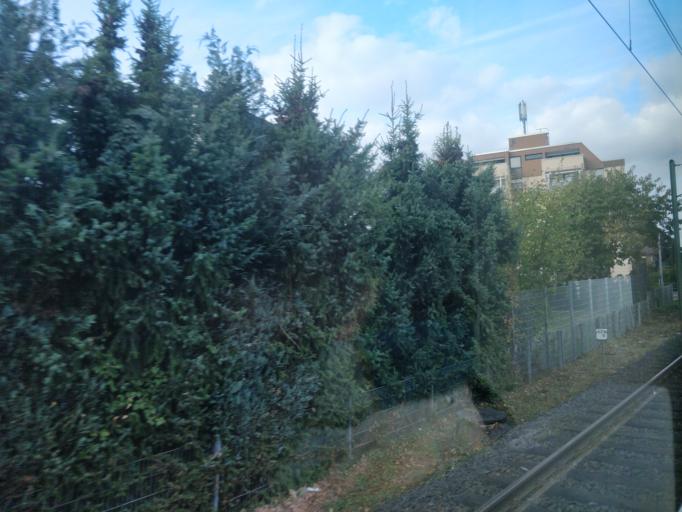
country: DE
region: North Rhine-Westphalia
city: Sankt Augustin
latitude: 50.7796
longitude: 7.1907
